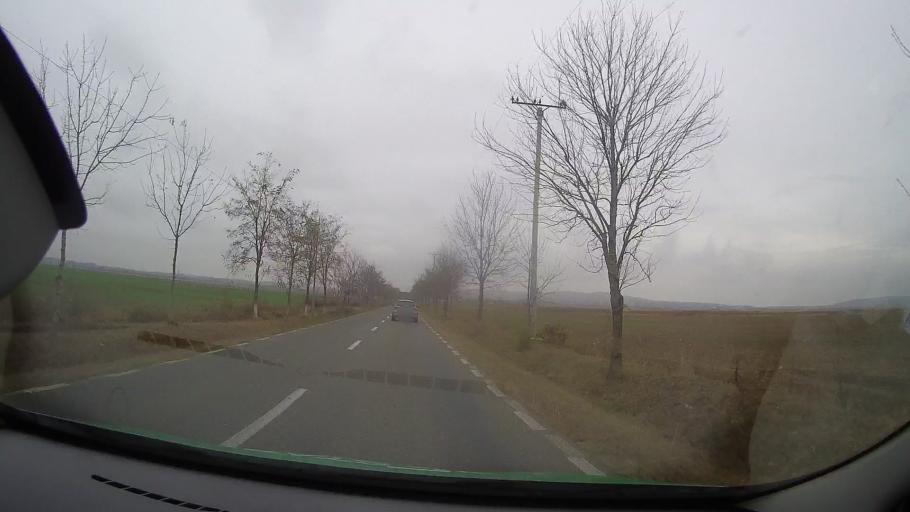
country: RO
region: Prahova
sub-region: Oras Baicoi
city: Liliesti
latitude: 45.0075
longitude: 25.8840
